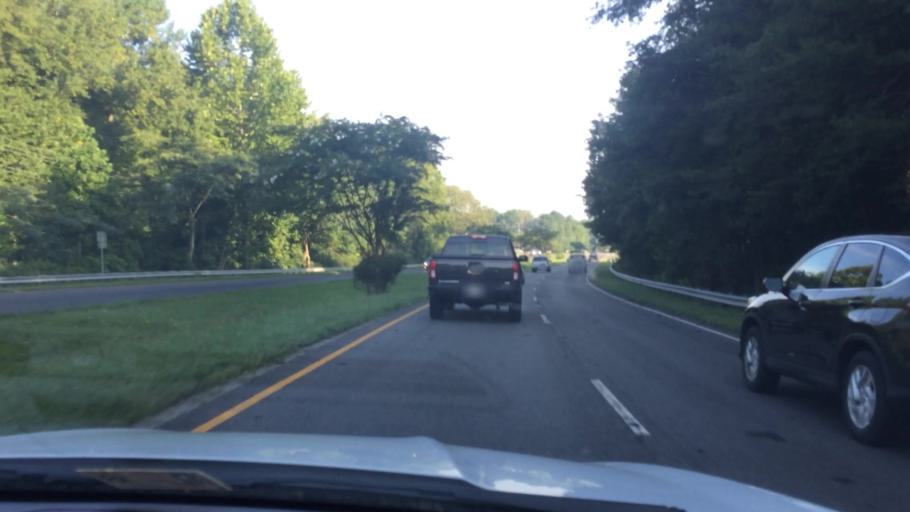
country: US
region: Virginia
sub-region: Gloucester County
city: Gloucester Courthouse
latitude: 37.3726
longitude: -76.5340
